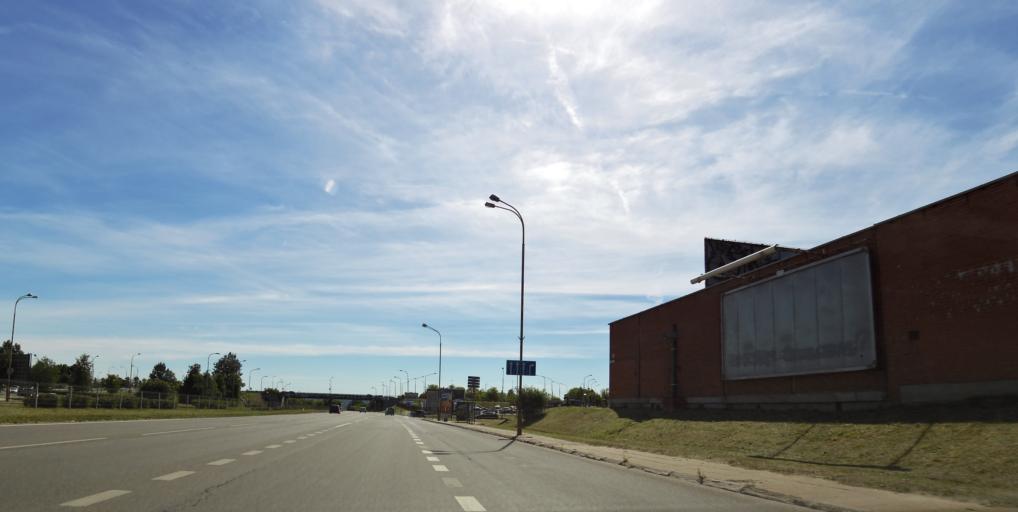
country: LT
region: Vilnius County
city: Seskine
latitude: 54.7124
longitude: 25.2491
